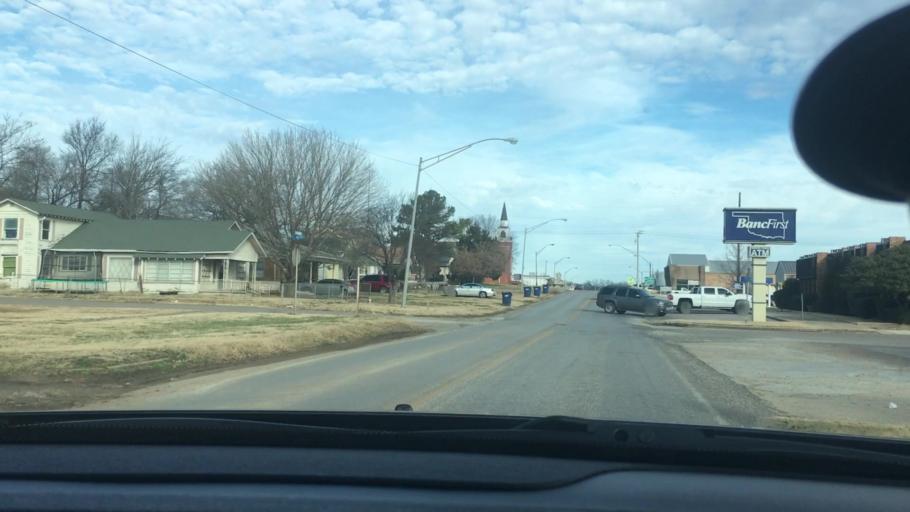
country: US
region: Oklahoma
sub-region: Seminole County
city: Konawa
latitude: 34.9544
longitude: -96.7521
